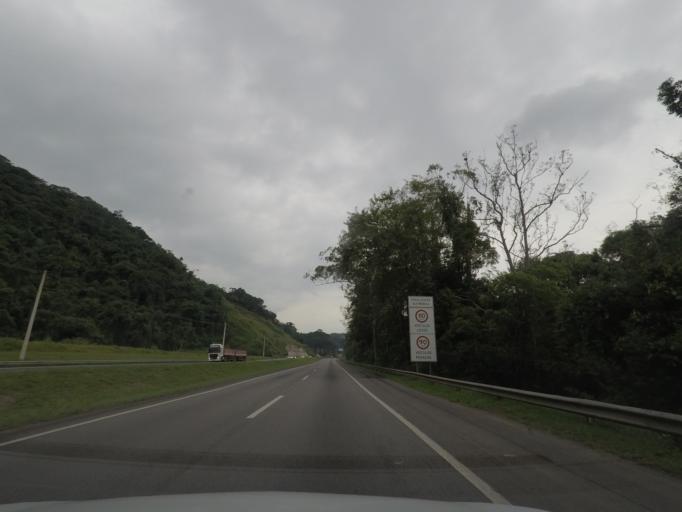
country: BR
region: Sao Paulo
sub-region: Miracatu
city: Miracatu
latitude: -24.1477
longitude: -47.3042
